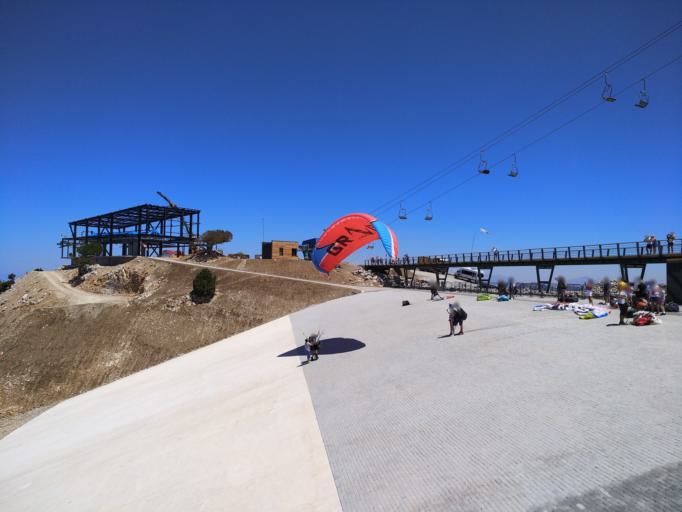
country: TR
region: Mugla
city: OEluedeniz
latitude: 36.5386
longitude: 29.1697
